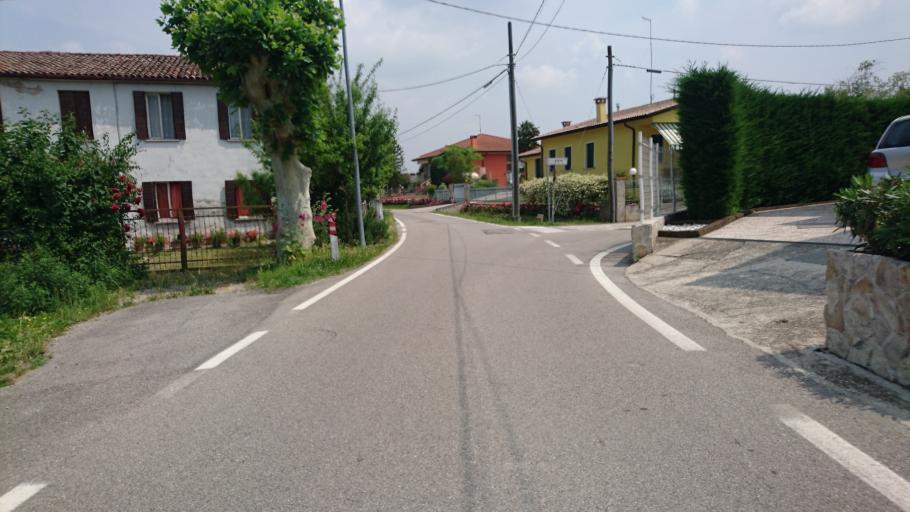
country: IT
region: Veneto
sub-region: Provincia di Padova
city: Cartura
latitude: 45.2692
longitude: 11.8648
